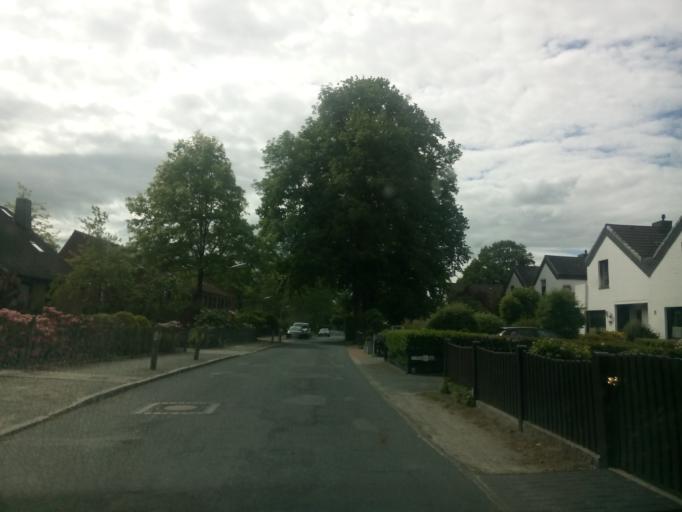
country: DE
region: Lower Saxony
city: Ritterhude
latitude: 53.1570
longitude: 8.7157
